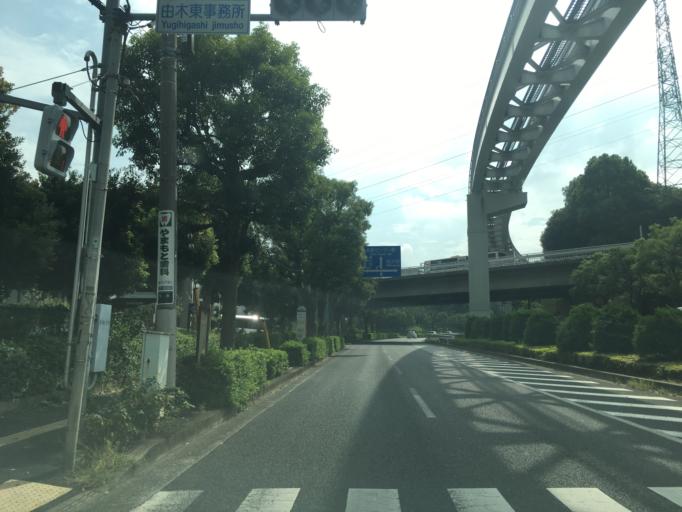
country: JP
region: Tokyo
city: Hino
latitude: 35.6343
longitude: 139.4205
